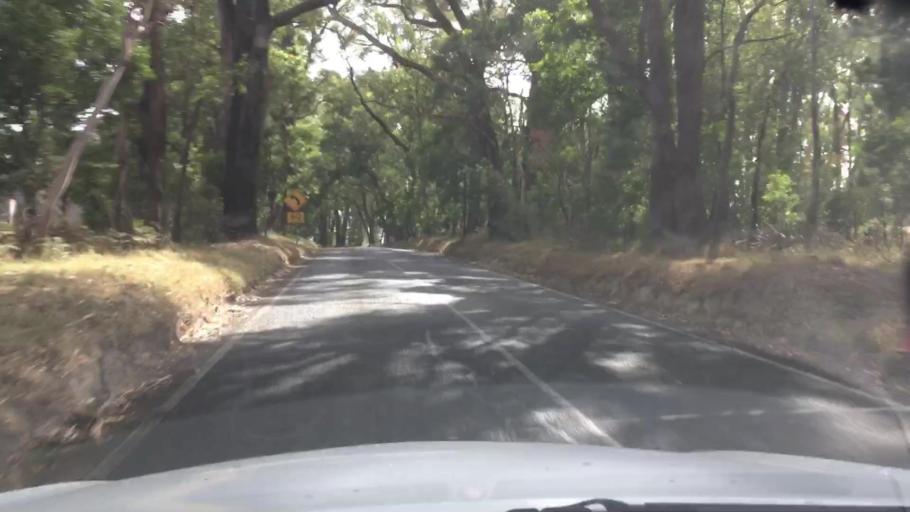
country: AU
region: Victoria
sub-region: Yarra Ranges
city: Macclesfield
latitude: -37.8260
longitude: 145.4920
